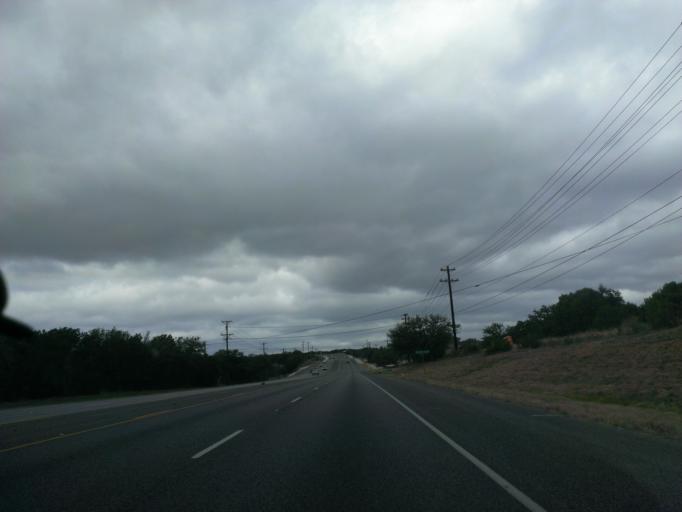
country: US
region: Texas
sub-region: Travis County
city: The Hills
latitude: 30.3410
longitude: -98.0428
